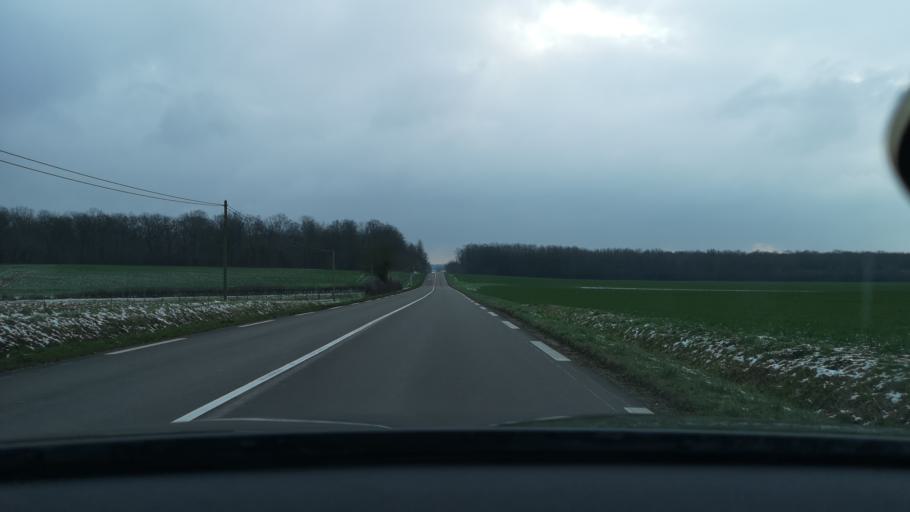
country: FR
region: Bourgogne
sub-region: Departement de Saone-et-Loire
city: Ouroux-sur-Saone
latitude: 46.7684
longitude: 4.9803
